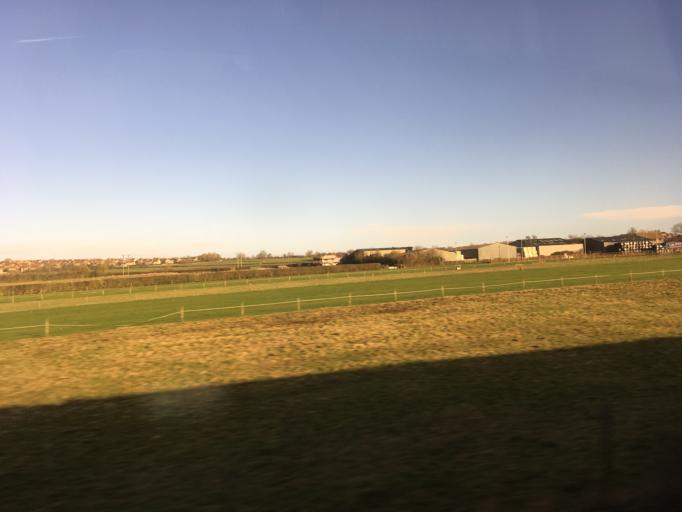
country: GB
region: England
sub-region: Wiltshire
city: Royal Wootton Bassett
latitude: 51.5361
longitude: -1.8774
